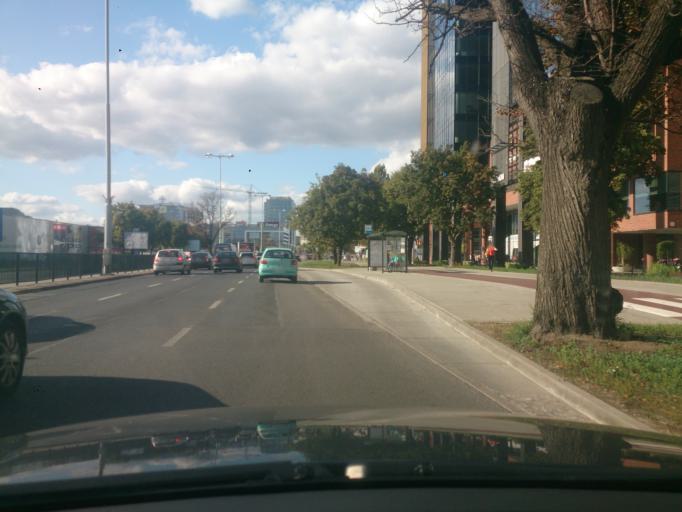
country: PL
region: Pomeranian Voivodeship
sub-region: Sopot
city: Sopot
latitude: 54.3984
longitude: 18.5764
